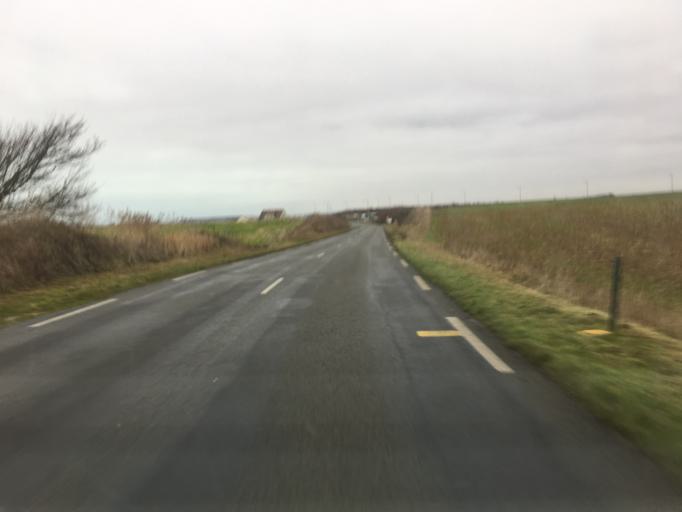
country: FR
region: Nord-Pas-de-Calais
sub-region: Departement du Pas-de-Calais
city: Equihen-Plage
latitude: 50.6877
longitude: 1.5760
